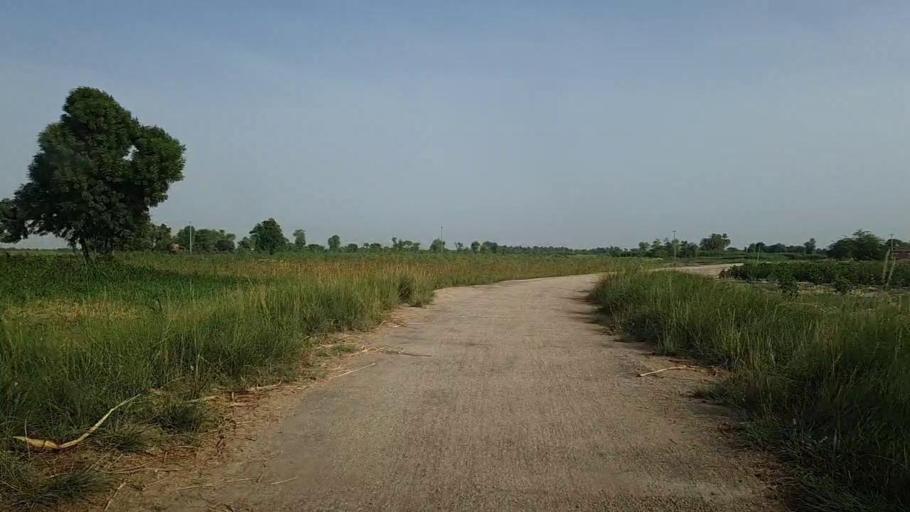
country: PK
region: Sindh
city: Pad Idan
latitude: 26.7526
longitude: 68.2573
